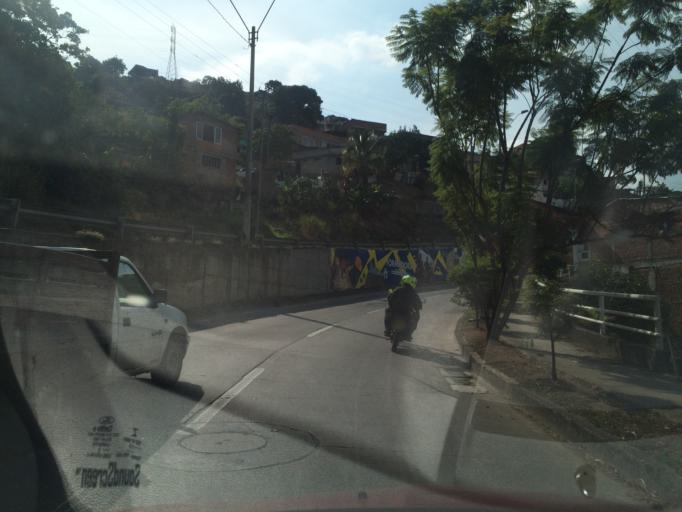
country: CO
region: Valle del Cauca
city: Cali
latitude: 3.4403
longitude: -76.5491
